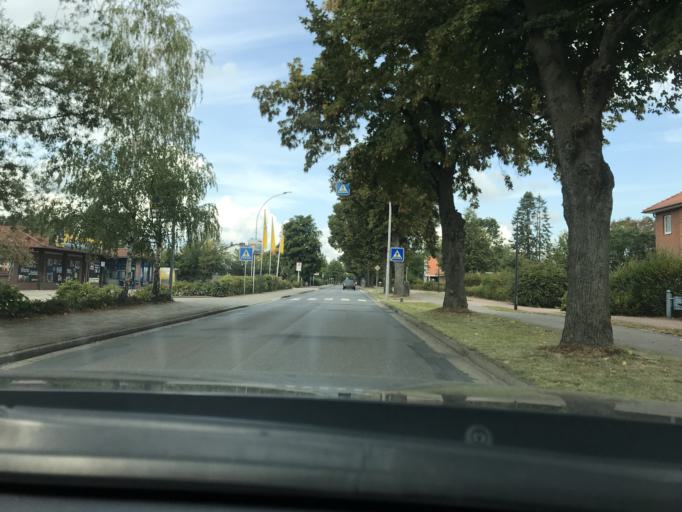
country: DE
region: Lower Saxony
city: Suderburg
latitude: 52.8994
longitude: 10.4400
